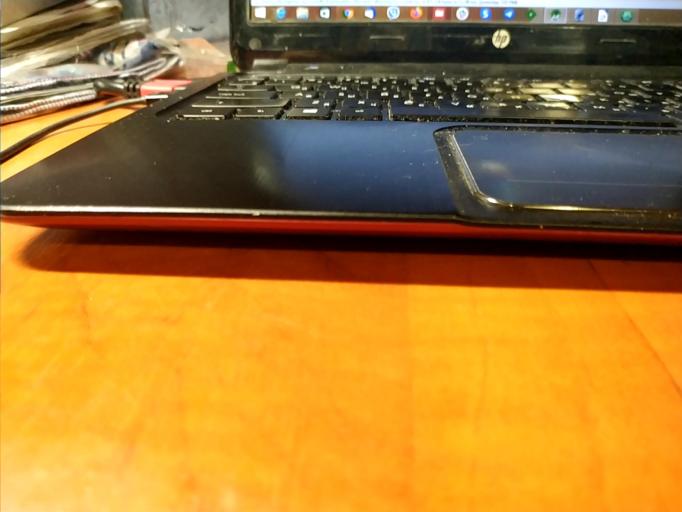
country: RU
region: Tverskaya
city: Ves'yegonsk
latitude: 58.7855
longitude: 37.5435
